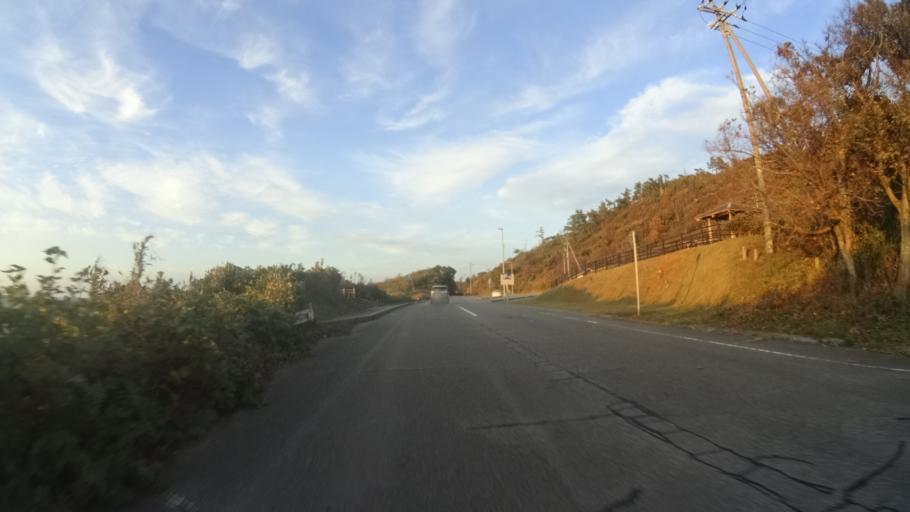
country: JP
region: Ishikawa
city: Nanao
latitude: 37.2169
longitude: 136.6960
